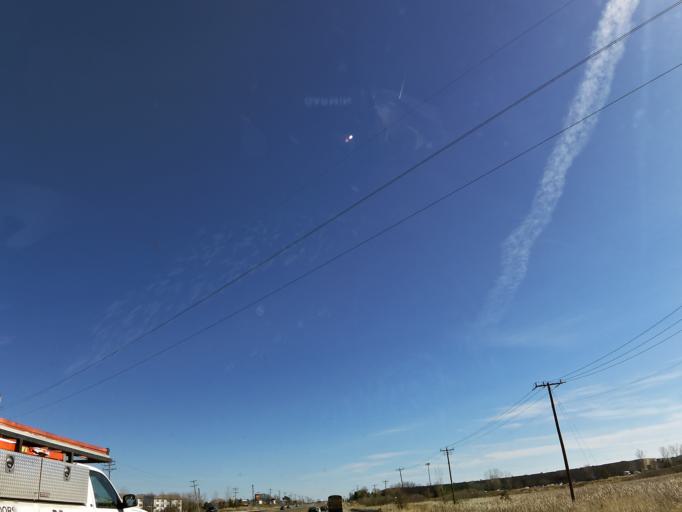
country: US
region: Minnesota
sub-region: Hennepin County
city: Plymouth
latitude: 45.0276
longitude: -93.5012
